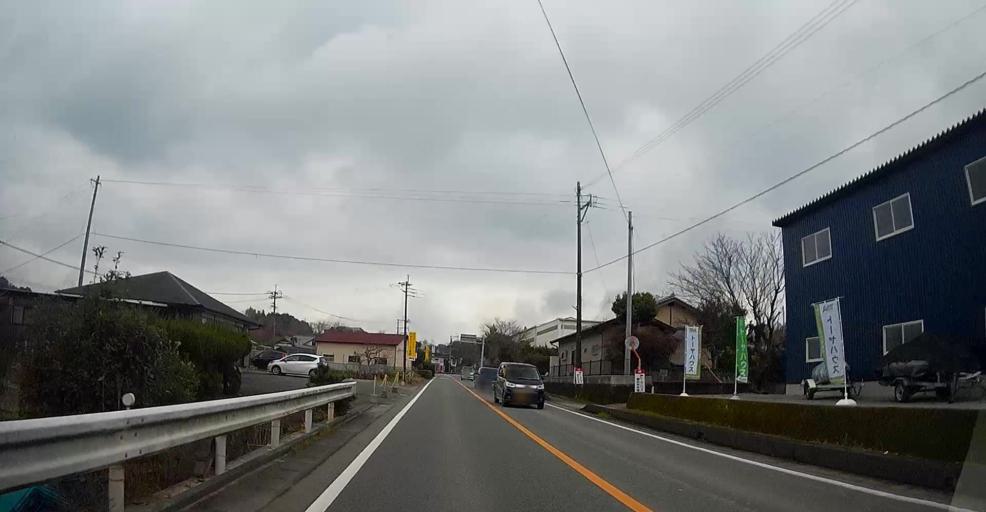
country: JP
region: Kumamoto
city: Matsubase
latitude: 32.6434
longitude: 130.7388
